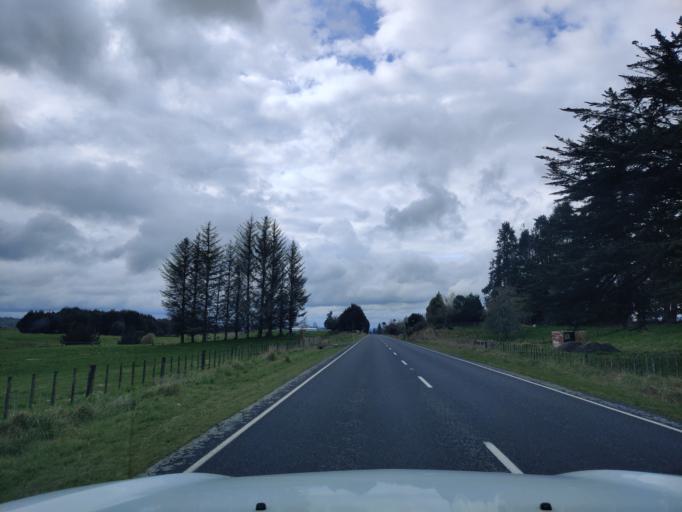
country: NZ
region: Waikato
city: Turangi
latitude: -39.0444
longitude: 175.3834
